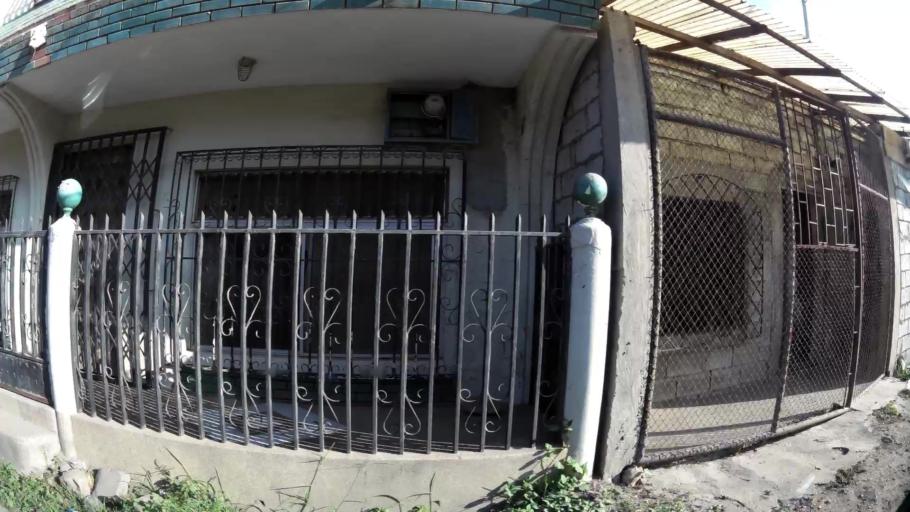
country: EC
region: Guayas
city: Guayaquil
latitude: -2.2263
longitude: -79.9100
